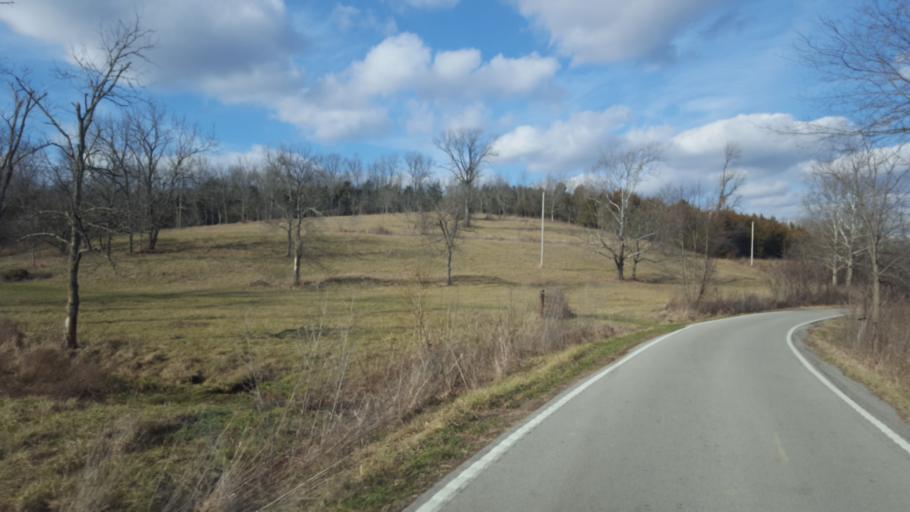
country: US
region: Kentucky
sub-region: Scott County
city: Georgetown
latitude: 38.3281
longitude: -84.5183
